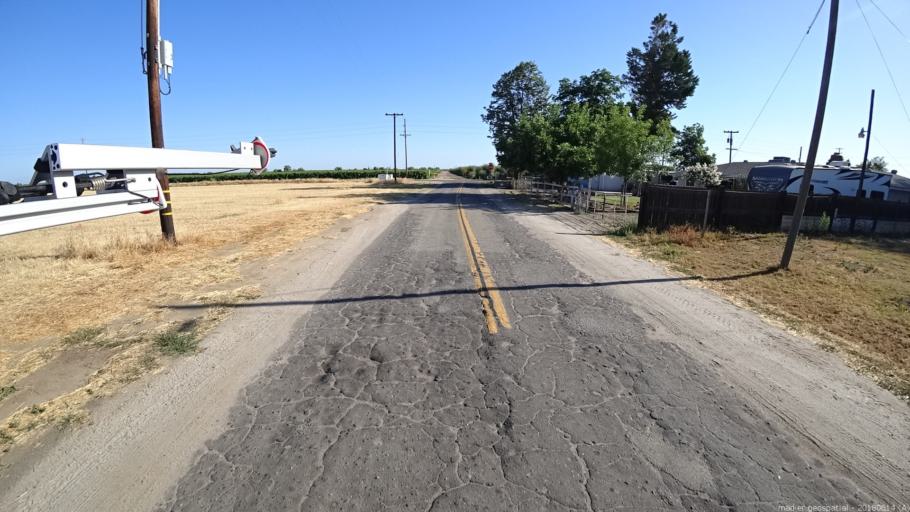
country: US
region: California
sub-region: Madera County
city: Madera
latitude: 36.9595
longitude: -120.1193
